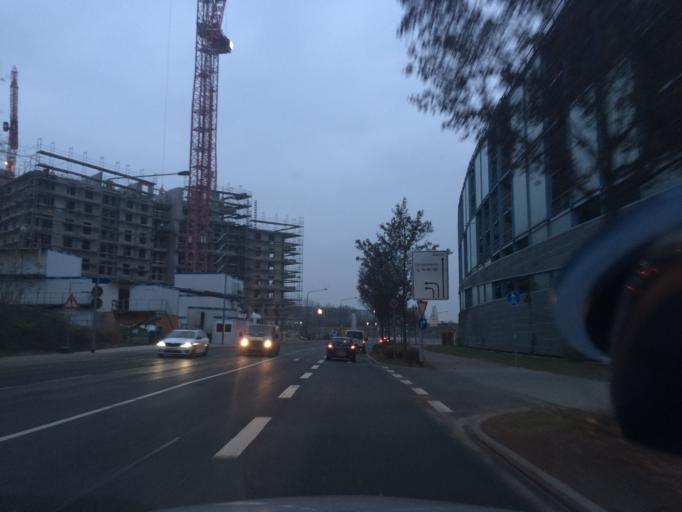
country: DE
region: Hesse
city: Niederrad
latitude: 50.1090
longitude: 8.6244
